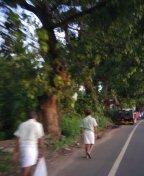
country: IN
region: Kerala
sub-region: Thrissur District
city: Trichur
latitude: 10.5391
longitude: 76.1846
